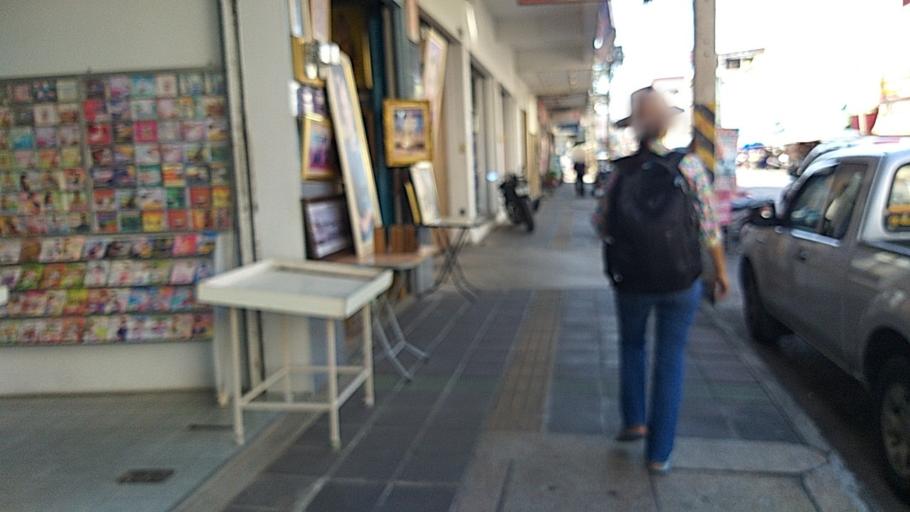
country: TH
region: Nakhon Ratchasima
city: Nakhon Ratchasima
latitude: 14.9750
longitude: 102.0965
